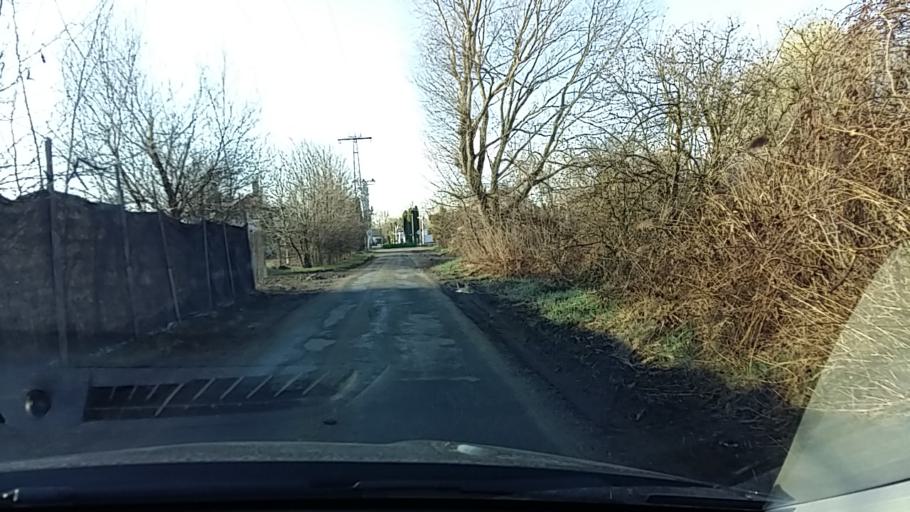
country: HU
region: Veszprem
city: Tapolca
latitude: 46.8747
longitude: 17.4383
